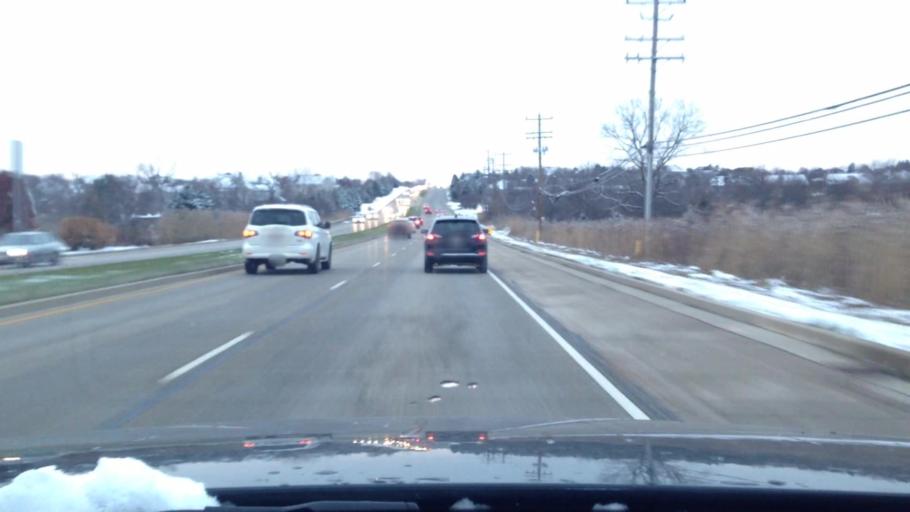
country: US
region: Illinois
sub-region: McHenry County
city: Lake in the Hills
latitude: 42.1758
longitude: -88.3456
